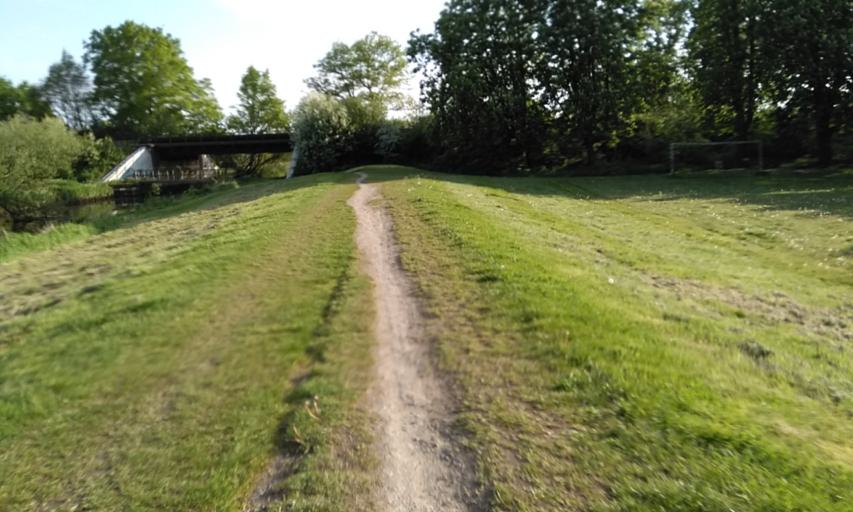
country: DE
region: Lower Saxony
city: Horneburg
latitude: 53.5046
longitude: 9.5834
